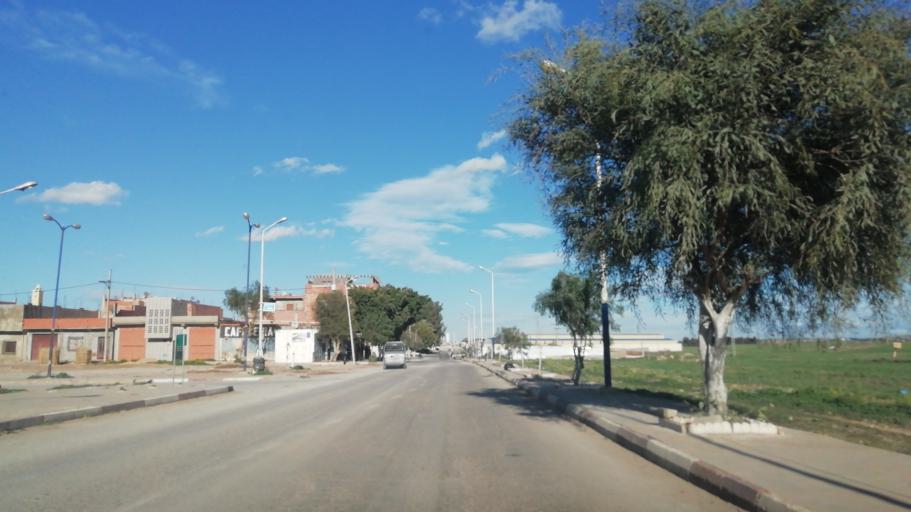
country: DZ
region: Oran
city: Sidi ech Chahmi
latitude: 35.6360
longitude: -0.5505
